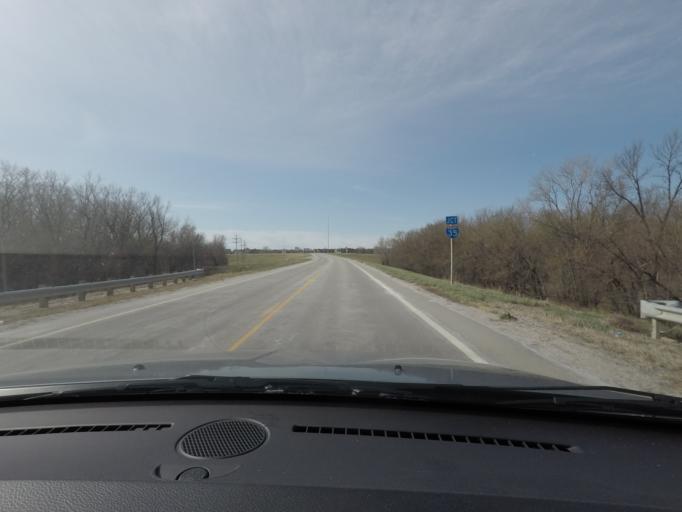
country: US
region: Kansas
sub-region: Lyon County
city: Emporia
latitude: 38.4272
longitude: -96.1805
